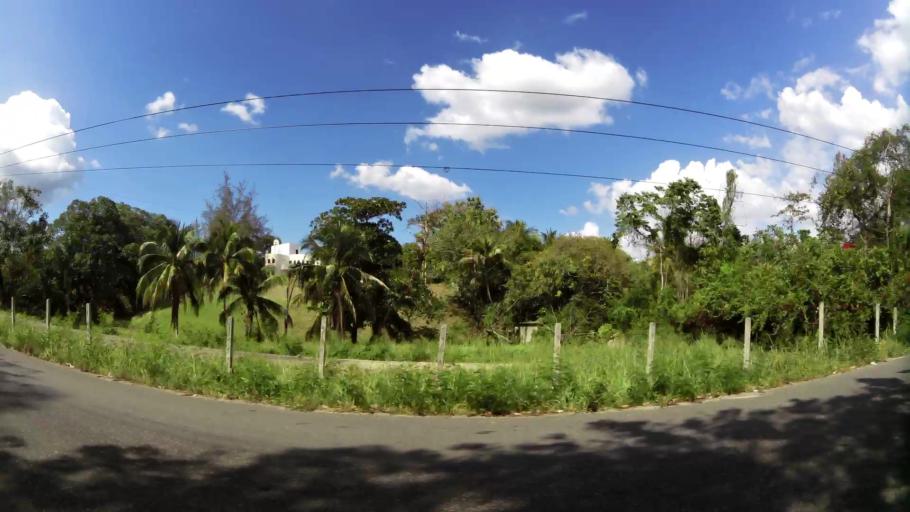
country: DO
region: San Cristobal
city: Bajos de Haina
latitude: 18.4269
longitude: -70.0578
